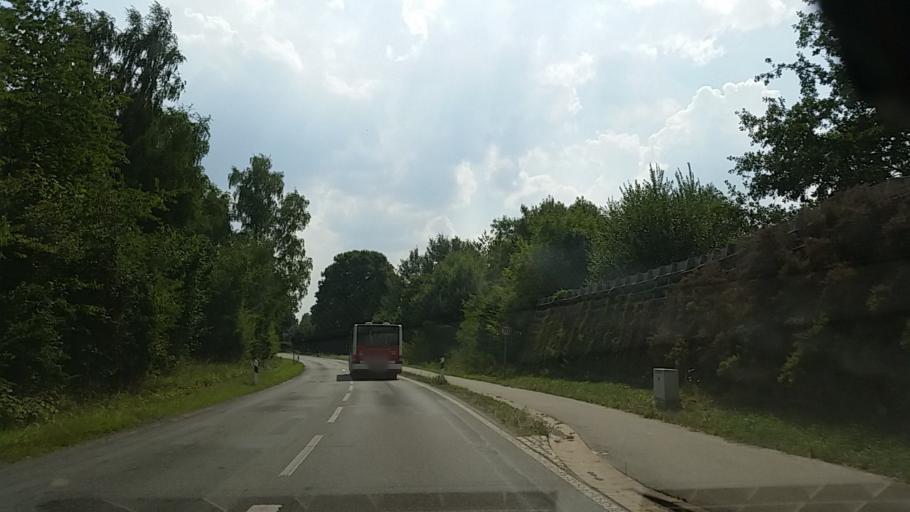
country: DE
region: Schleswig-Holstein
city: Schmilau
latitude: 53.6802
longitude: 10.7721
